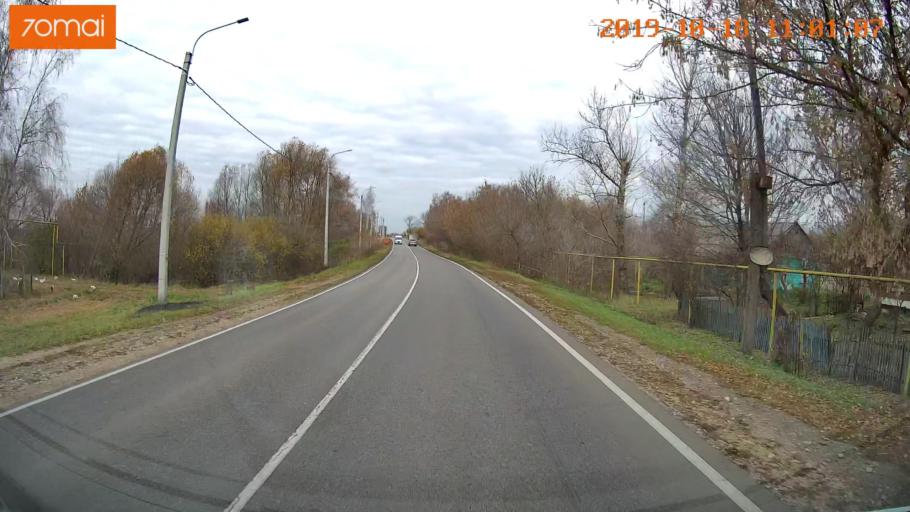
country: RU
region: Tula
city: Yepifan'
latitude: 53.8510
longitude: 38.5527
